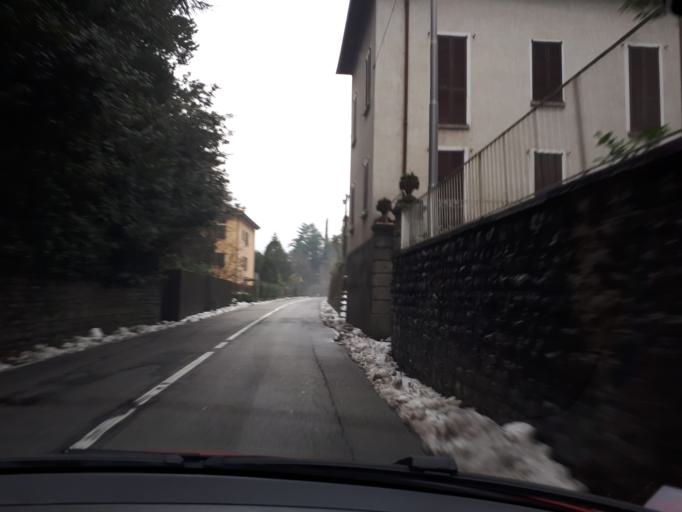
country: IT
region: Lombardy
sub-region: Provincia di Lecco
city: Lierna
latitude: 45.9679
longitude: 9.3031
